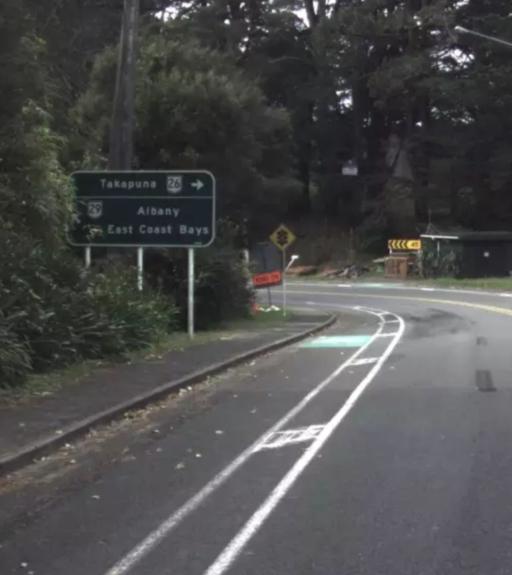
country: NZ
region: Auckland
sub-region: Auckland
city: Rothesay Bay
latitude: -36.7622
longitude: 174.7065
